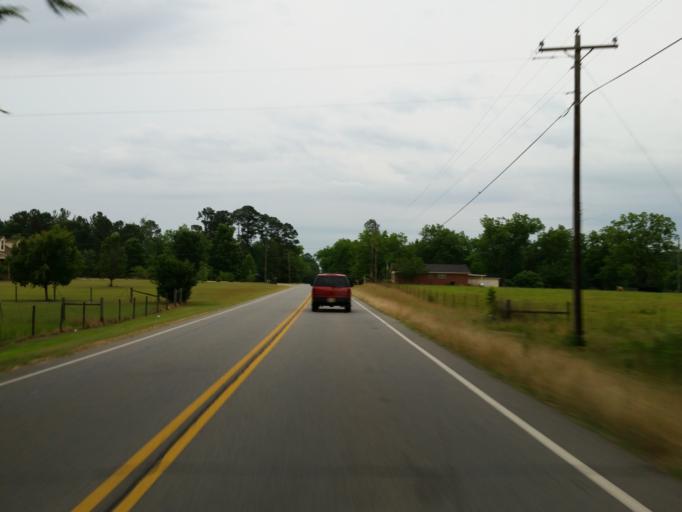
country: US
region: Georgia
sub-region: Dooly County
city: Vienna
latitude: 32.1215
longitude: -83.7982
